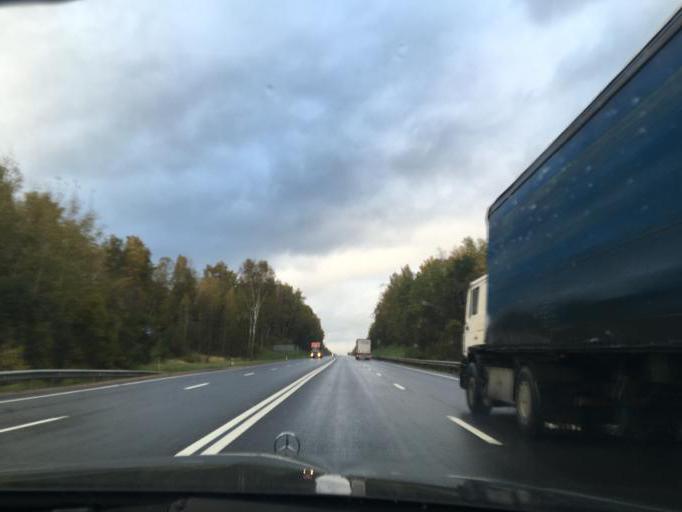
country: RU
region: Smolensk
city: Pechersk
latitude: 54.8864
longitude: 32.0872
